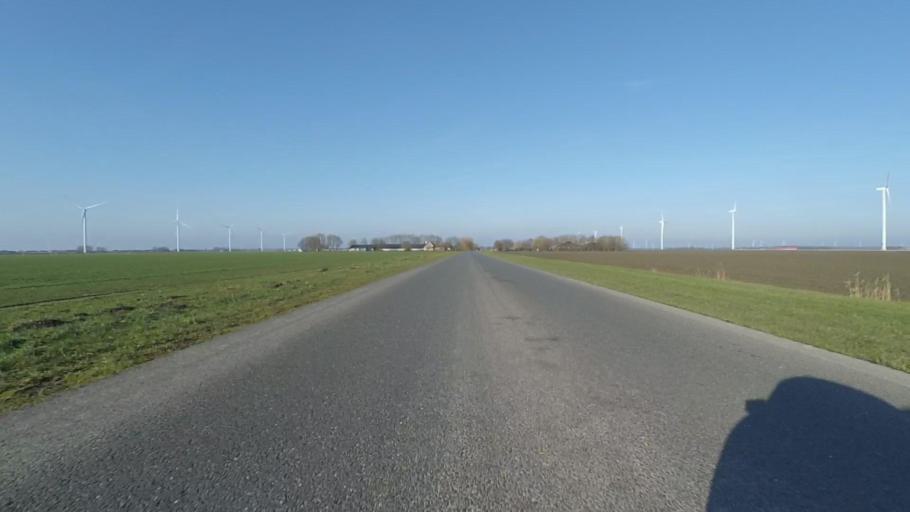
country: NL
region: Utrecht
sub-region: Gemeente Bunschoten
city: Spakenburg
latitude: 52.2901
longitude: 5.3958
